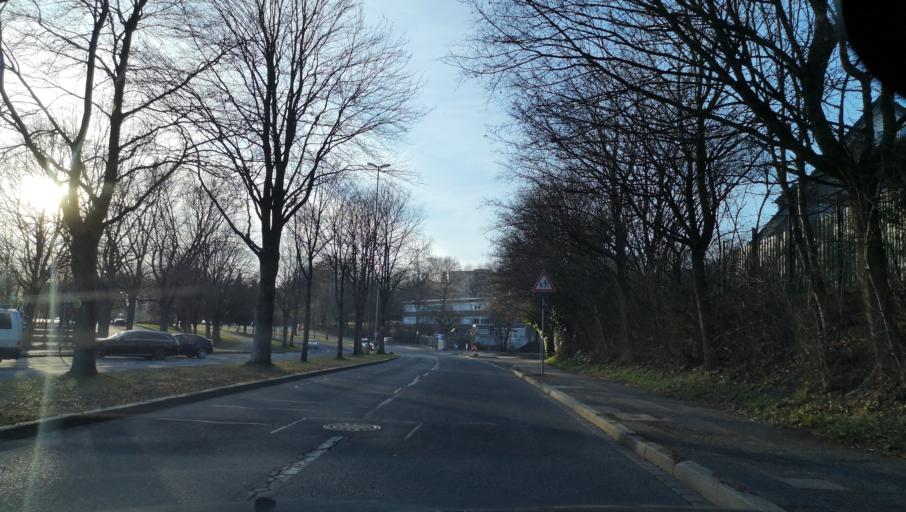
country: DE
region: North Rhine-Westphalia
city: Radevormwald
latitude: 51.2002
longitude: 7.2798
